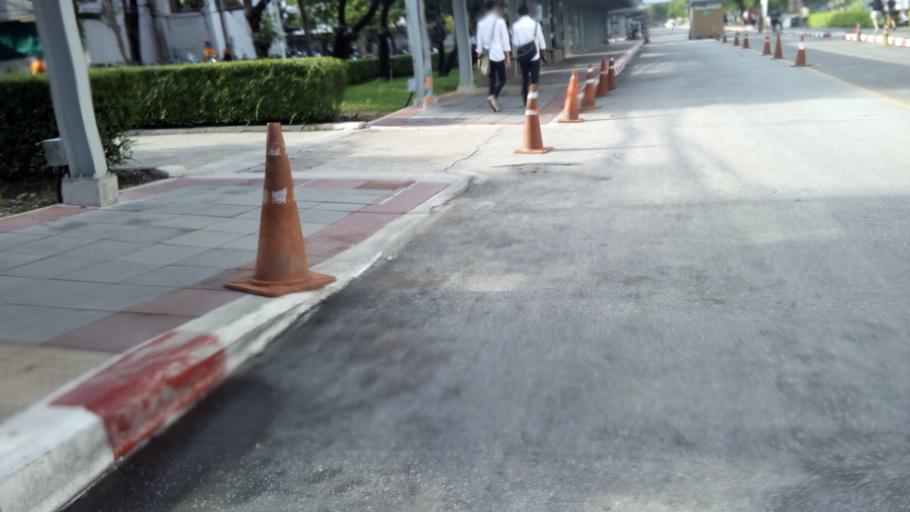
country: TH
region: Nakhon Nayok
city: Ongkharak
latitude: 14.1060
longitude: 100.9882
